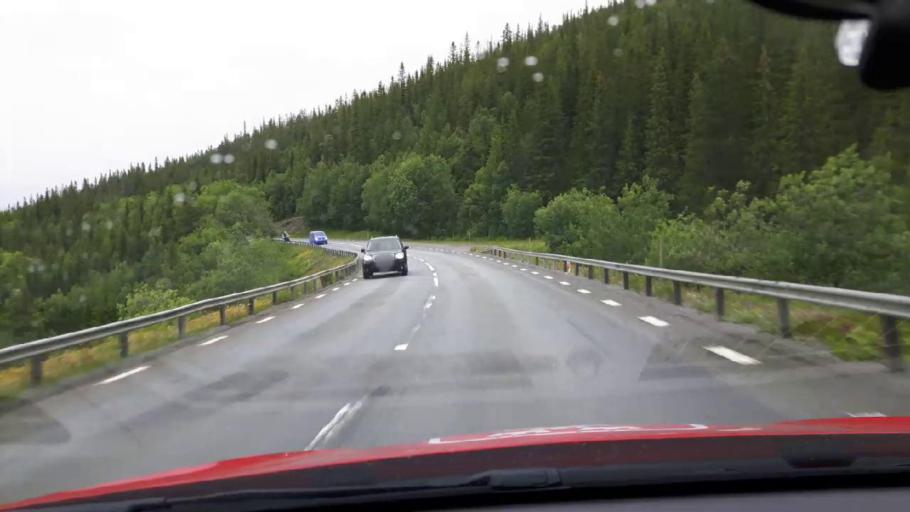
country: NO
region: Nord-Trondelag
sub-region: Meraker
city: Meraker
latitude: 63.3349
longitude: 12.0619
